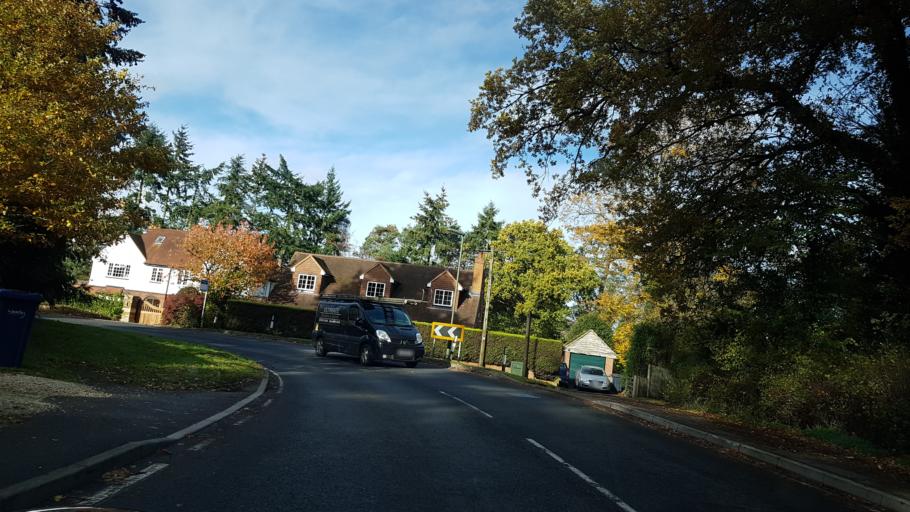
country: GB
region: England
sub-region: Hampshire
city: Aldershot
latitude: 51.2182
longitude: -0.7533
